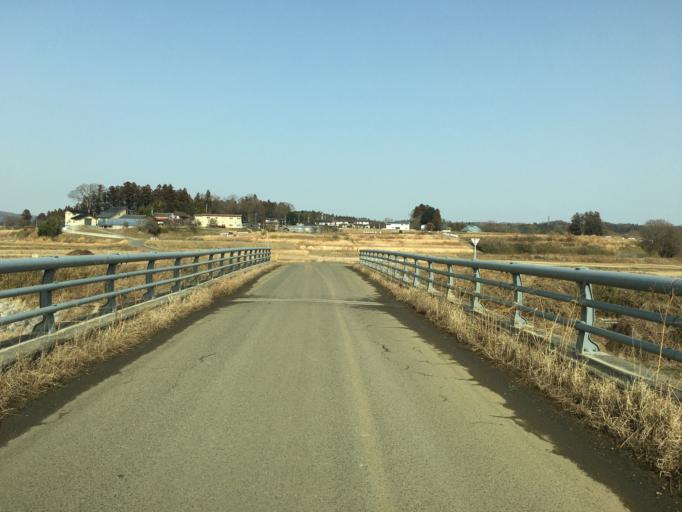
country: JP
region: Fukushima
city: Nihommatsu
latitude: 37.5583
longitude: 140.3977
